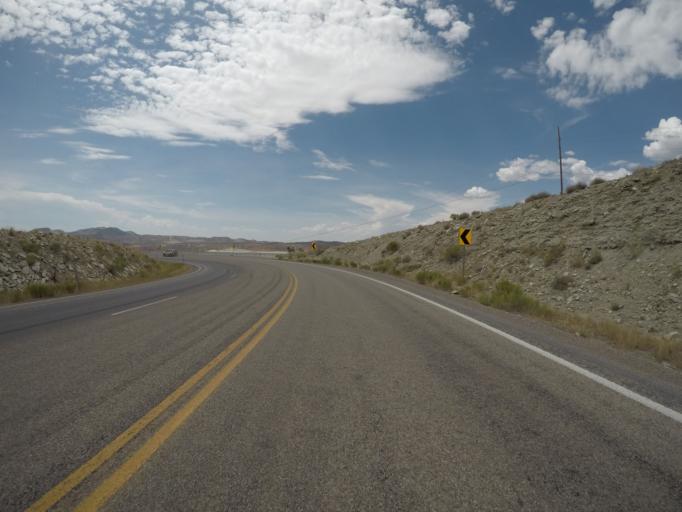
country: US
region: Utah
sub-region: Uintah County
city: Vernal
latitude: 40.6150
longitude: -109.4776
